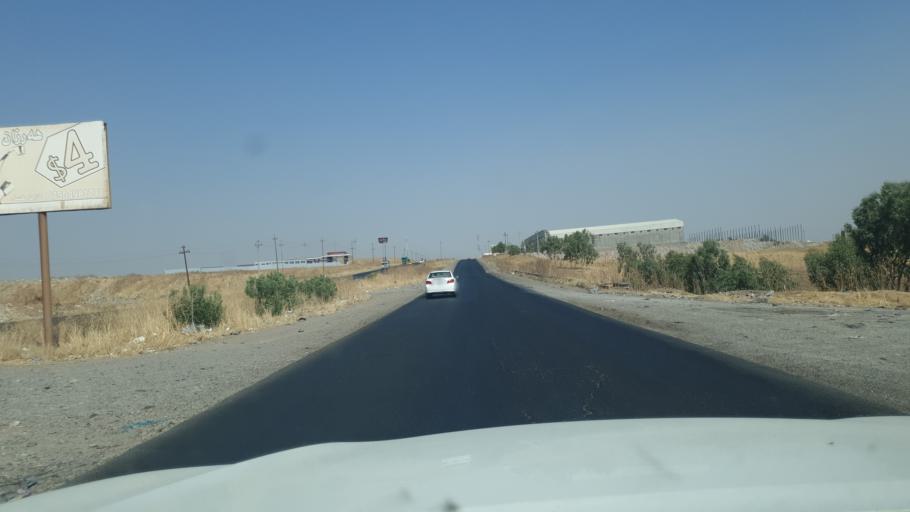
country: IQ
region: Arbil
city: Erbil
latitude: 36.1969
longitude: 43.8920
